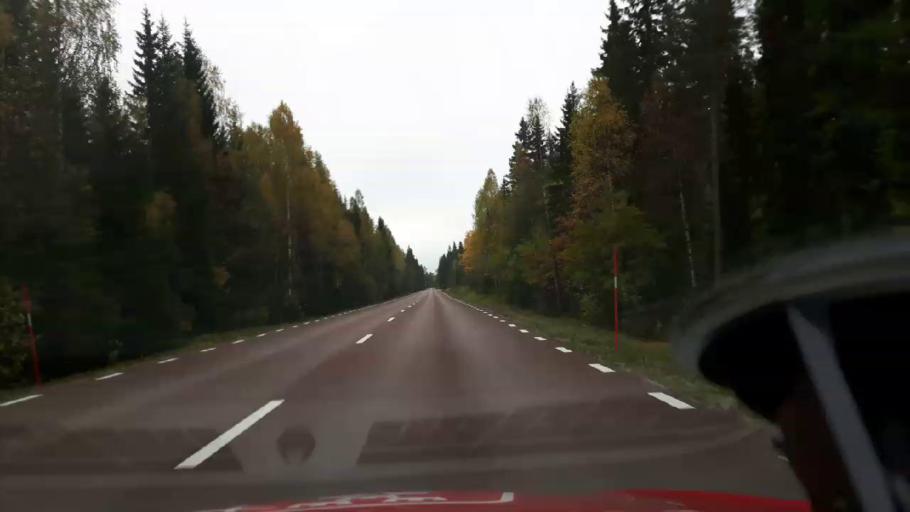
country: SE
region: Jaemtland
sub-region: Harjedalens Kommun
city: Sveg
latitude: 62.3340
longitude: 14.7321
